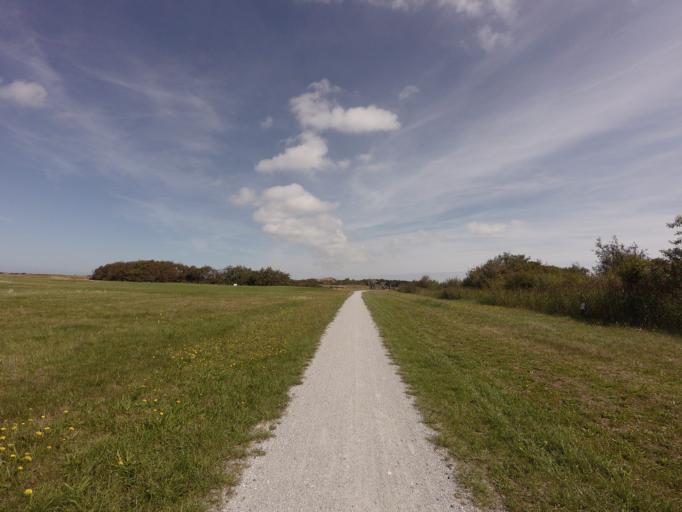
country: NL
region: Friesland
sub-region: Gemeente Ameland
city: Hollum
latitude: 53.4476
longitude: 5.6543
